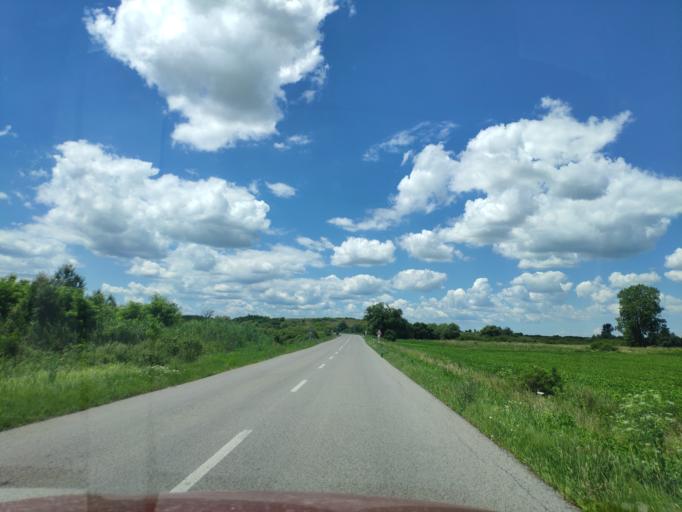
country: HU
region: Borsod-Abauj-Zemplen
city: Ozd
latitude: 48.3096
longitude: 20.2537
